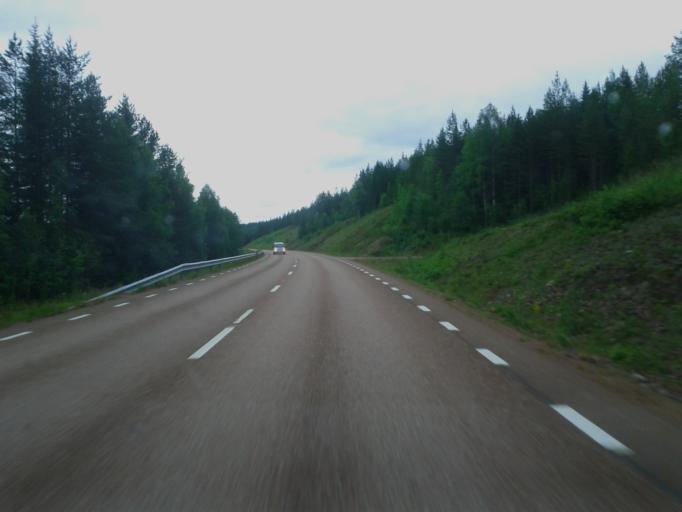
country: SE
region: Dalarna
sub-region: Alvdalens Kommun
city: AElvdalen
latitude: 61.2744
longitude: 13.9134
